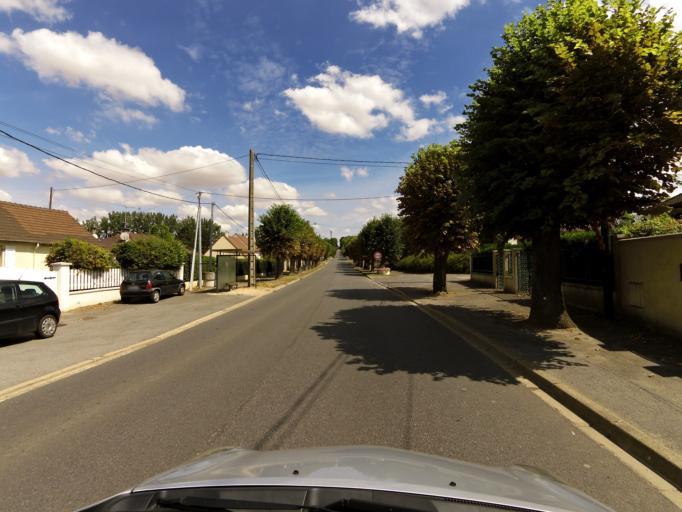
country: FR
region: Ile-de-France
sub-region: Departement de Seine-et-Marne
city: Varreddes
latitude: 49.0060
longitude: 2.9319
